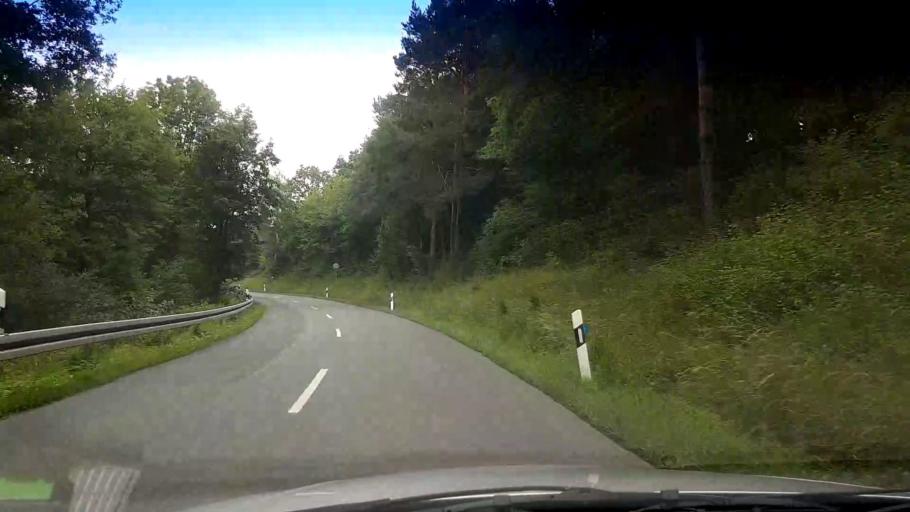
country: DE
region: Bavaria
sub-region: Upper Franconia
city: Mainleus
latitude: 50.0884
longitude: 11.3494
